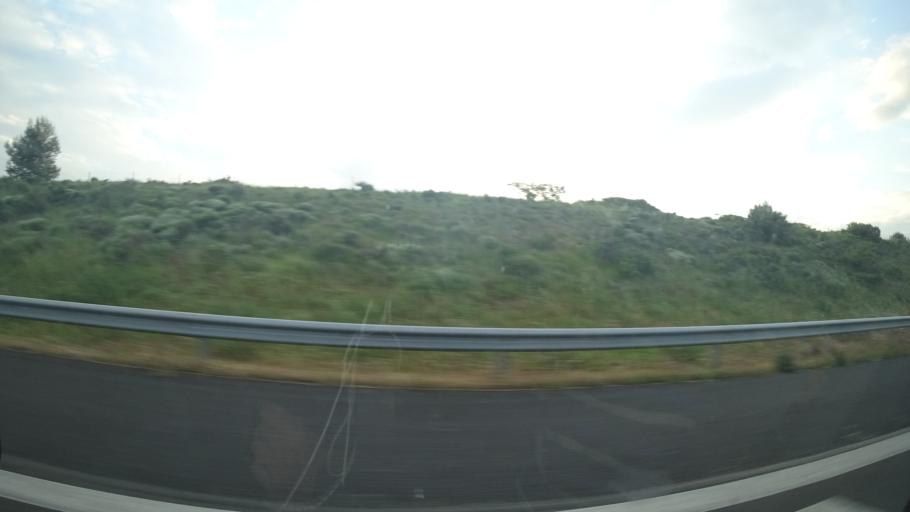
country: FR
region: Languedoc-Roussillon
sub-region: Departement de l'Herault
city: Paulhan
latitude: 43.5283
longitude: 3.4434
